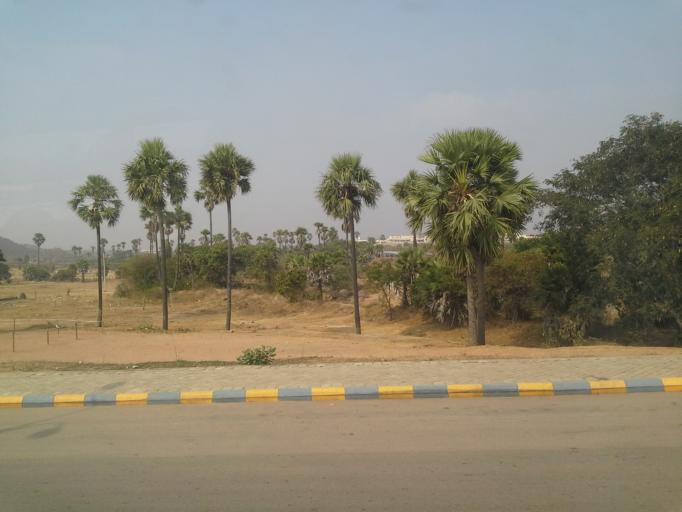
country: IN
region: Telangana
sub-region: Rangareddi
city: Lal Bahadur Nagar
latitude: 17.3103
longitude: 78.6820
